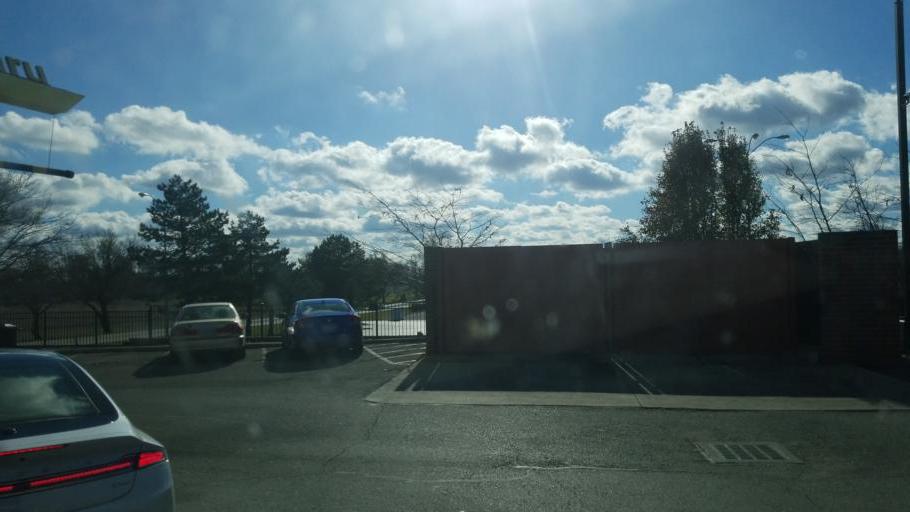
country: US
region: Ohio
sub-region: Hardin County
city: Kenton
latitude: 40.6514
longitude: -83.5910
